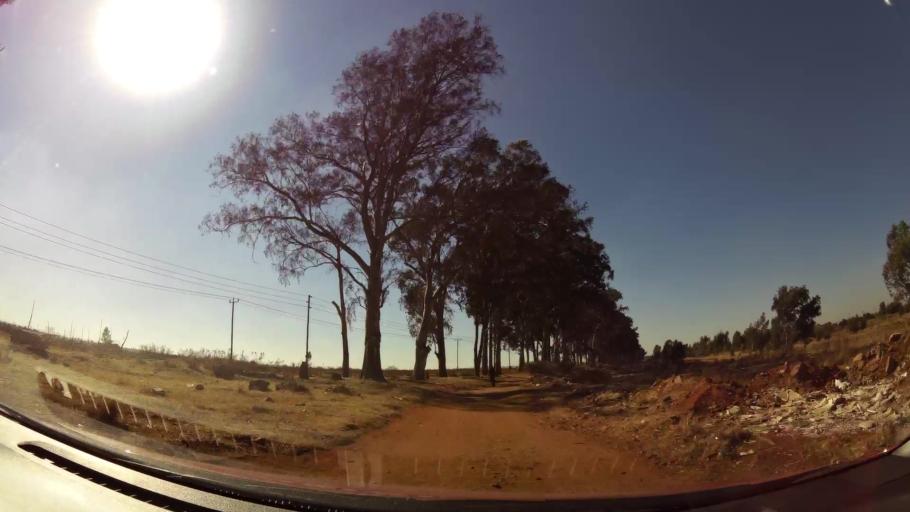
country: ZA
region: Gauteng
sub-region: City of Johannesburg Metropolitan Municipality
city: Soweto
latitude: -26.2160
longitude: 27.8443
